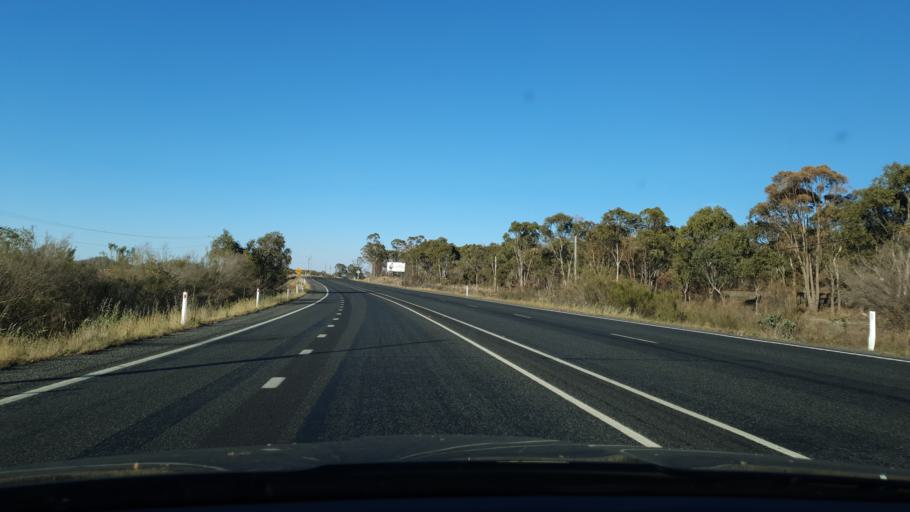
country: AU
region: Queensland
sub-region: Southern Downs
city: Stanthorpe
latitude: -28.6885
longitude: 151.9109
